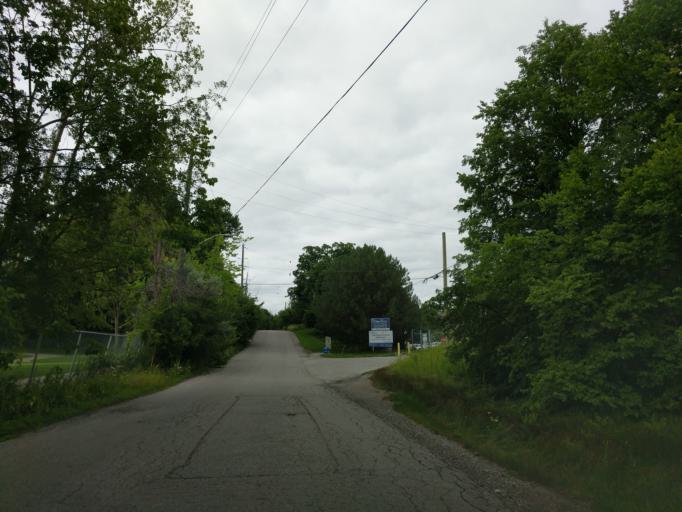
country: CA
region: Ontario
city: Willowdale
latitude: 43.8118
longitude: -79.3740
